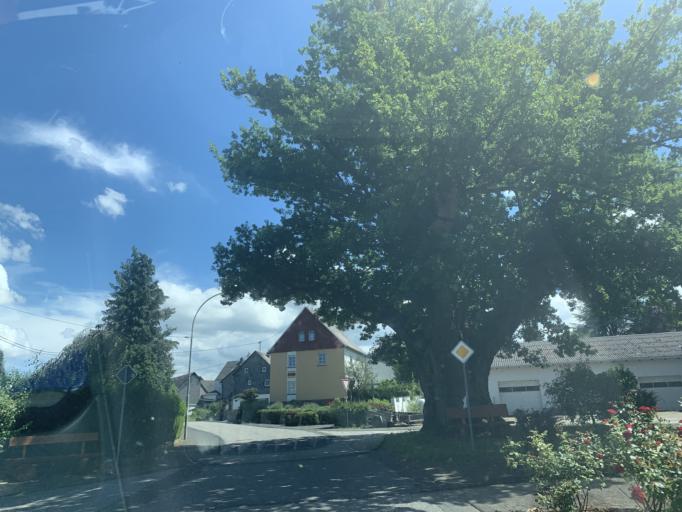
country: DE
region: Rheinland-Pfalz
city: Buch
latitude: 50.0776
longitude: 7.3836
